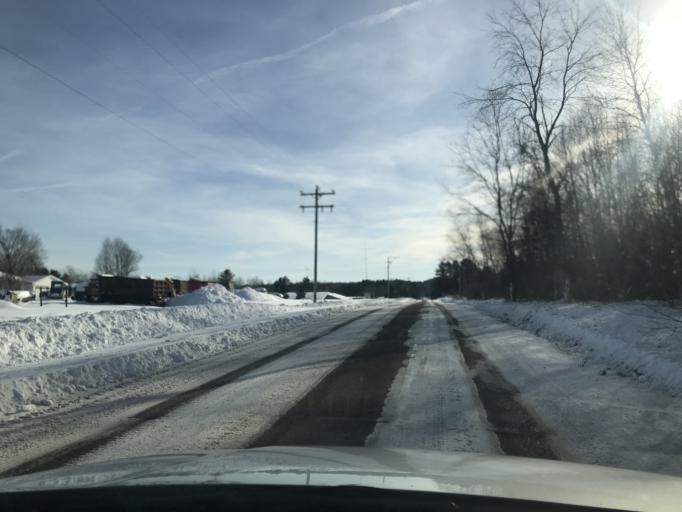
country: US
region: Wisconsin
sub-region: Menominee County
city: Legend Lake
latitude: 45.3101
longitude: -88.5219
